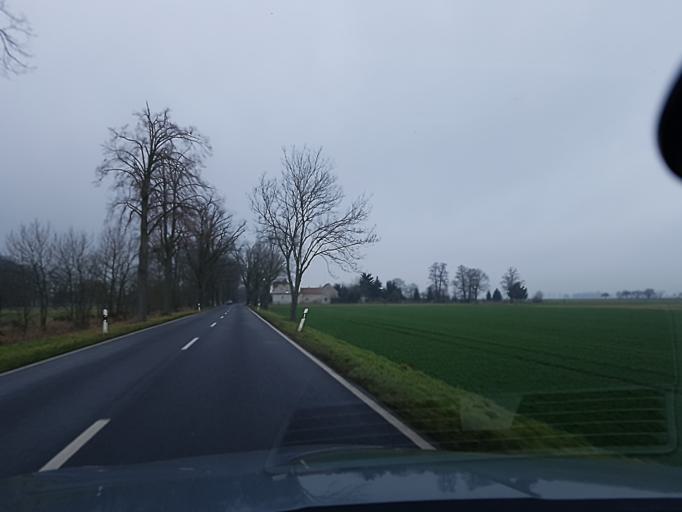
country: DE
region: Brandenburg
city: Doberlug-Kirchhain
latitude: 51.6487
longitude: 13.5525
